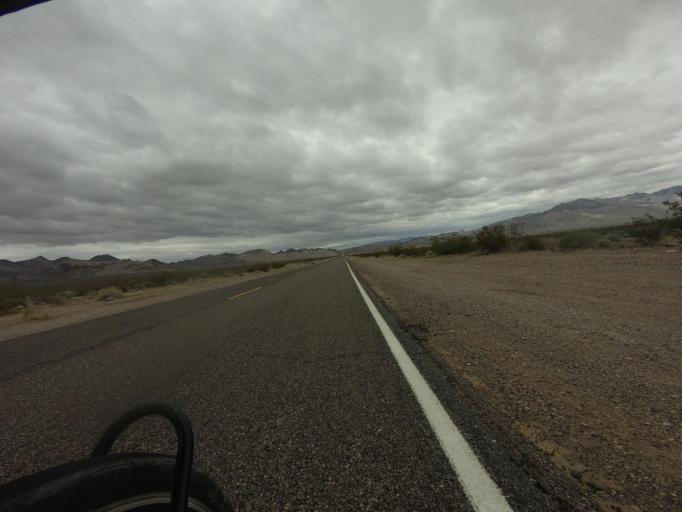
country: US
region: Nevada
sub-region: Nye County
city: Beatty
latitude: 36.8594
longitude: -116.8455
